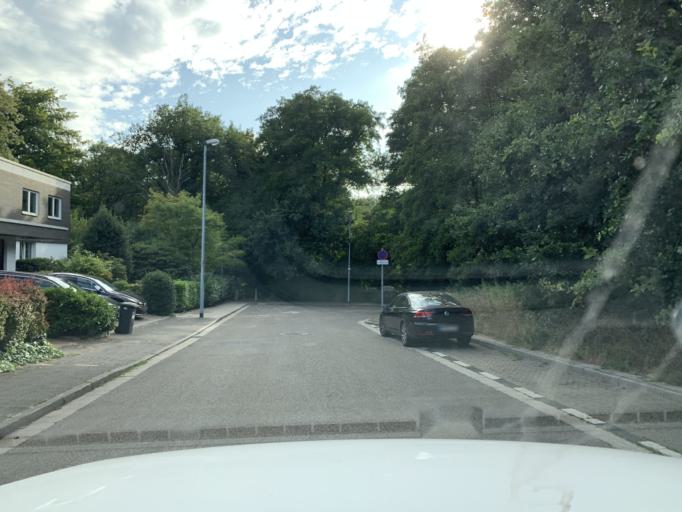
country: DE
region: North Rhine-Westphalia
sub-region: Regierungsbezirk Dusseldorf
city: Muelheim (Ruhr)
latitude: 51.4152
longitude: 6.8482
